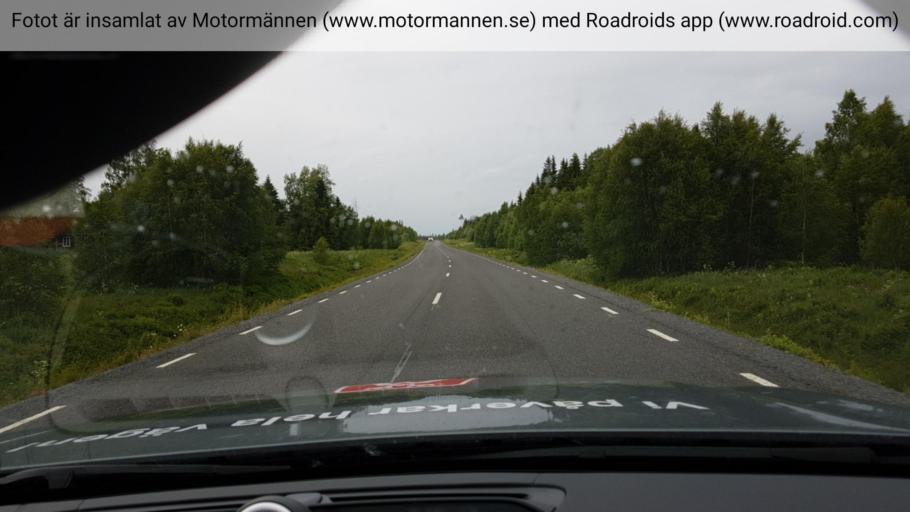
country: SE
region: Jaemtland
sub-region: Stroemsunds Kommun
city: Stroemsund
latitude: 63.6389
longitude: 15.1897
